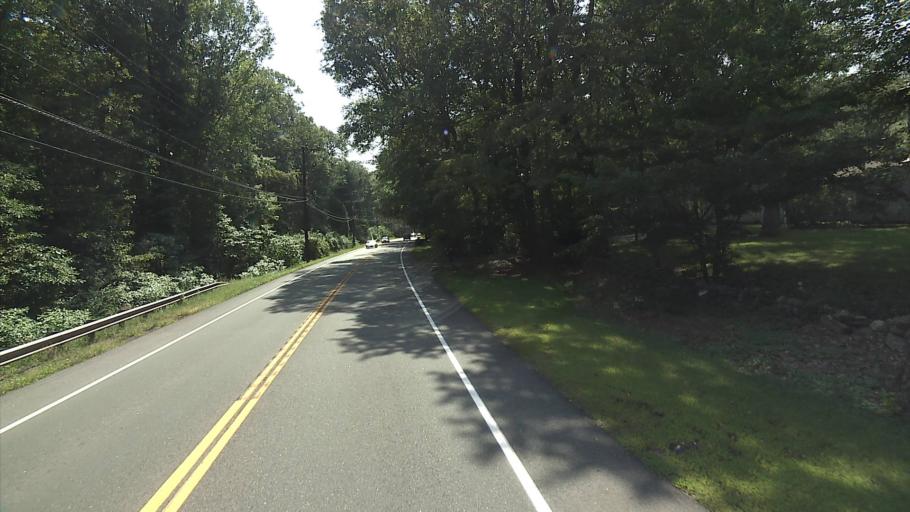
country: US
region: Connecticut
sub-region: New Haven County
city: Madison Center
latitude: 41.3184
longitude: -72.6078
